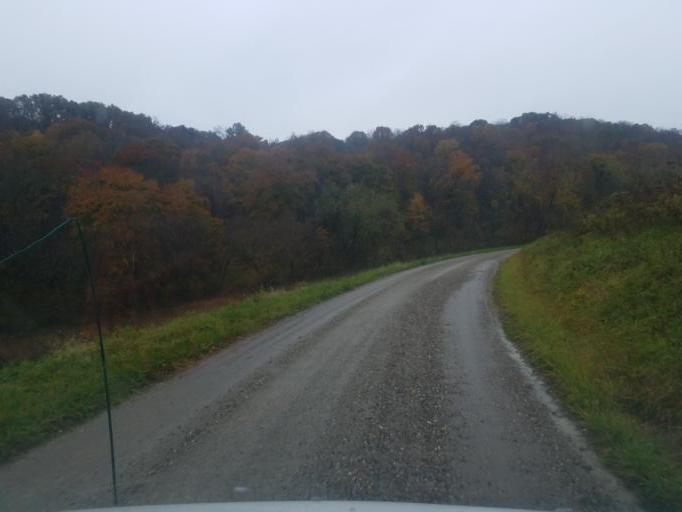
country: US
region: Ohio
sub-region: Washington County
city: Beverly
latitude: 39.4705
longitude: -81.7493
